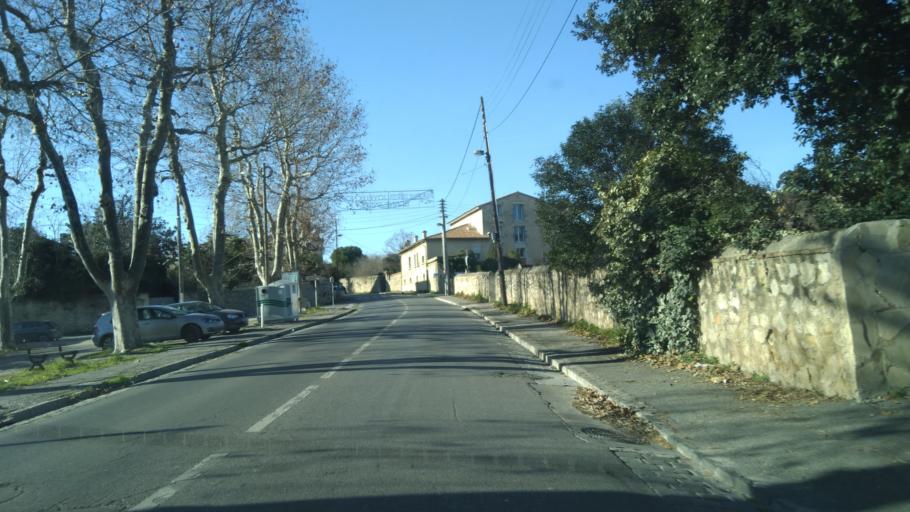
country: FR
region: Provence-Alpes-Cote d'Azur
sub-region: Departement des Bouches-du-Rhone
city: Marseille 12
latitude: 43.3031
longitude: 5.4478
